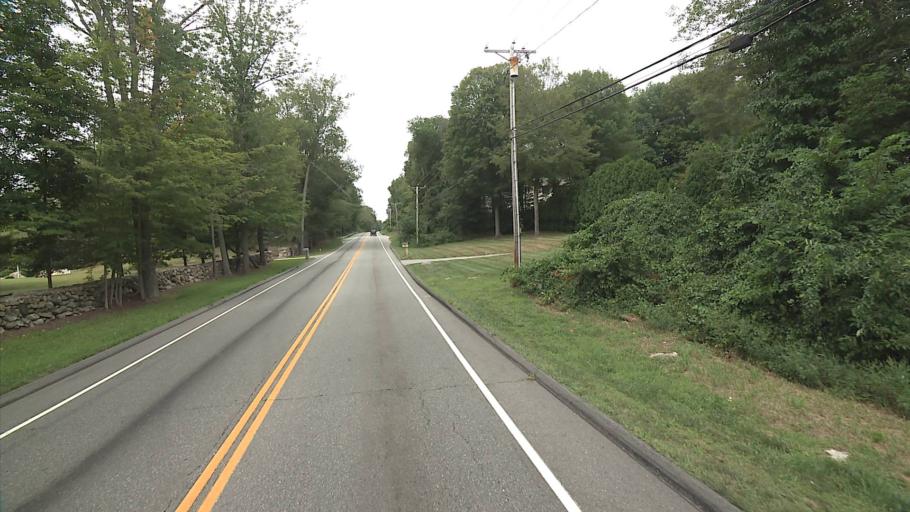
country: US
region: Connecticut
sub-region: New London County
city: Montville Center
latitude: 41.4427
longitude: -72.2293
